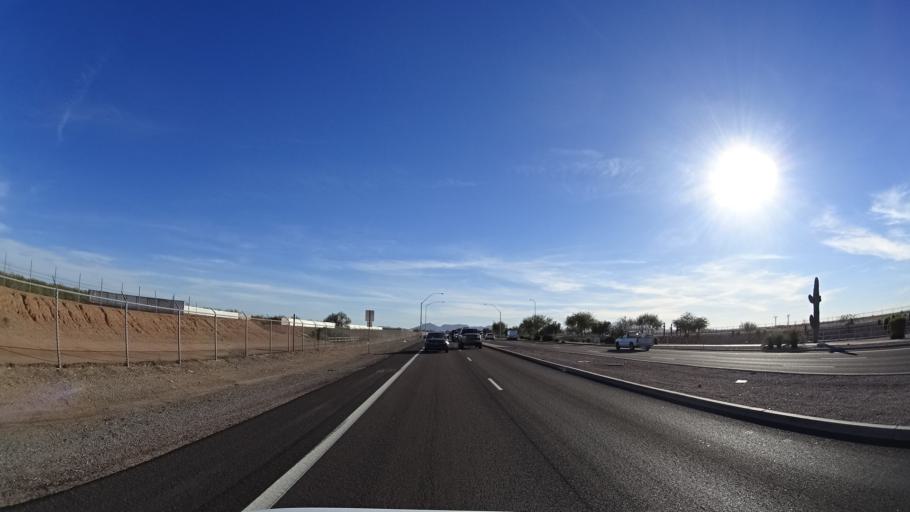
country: US
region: Arizona
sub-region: Maricopa County
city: Queen Creek
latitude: 33.3080
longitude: -111.6352
